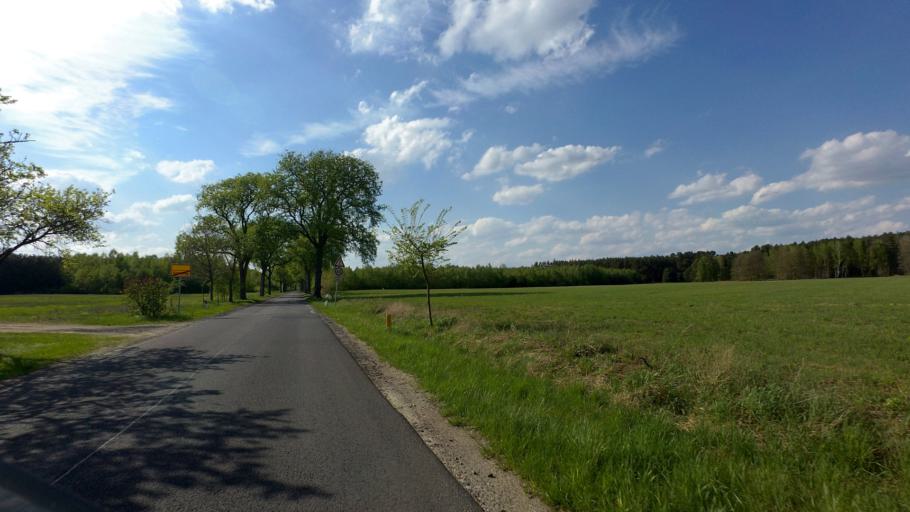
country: DE
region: Brandenburg
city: Templin
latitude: 53.0032
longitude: 13.4731
